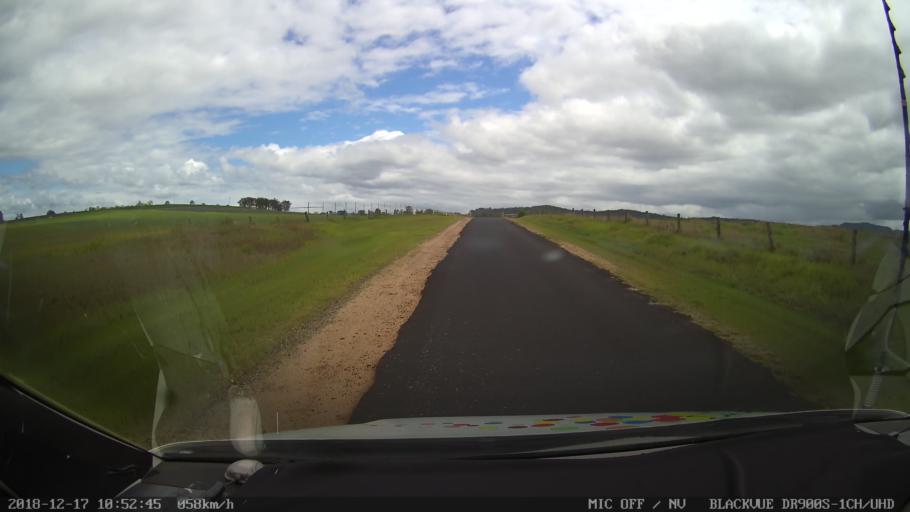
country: AU
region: New South Wales
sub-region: Tenterfield Municipality
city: Carrolls Creek
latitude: -28.8424
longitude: 152.5627
